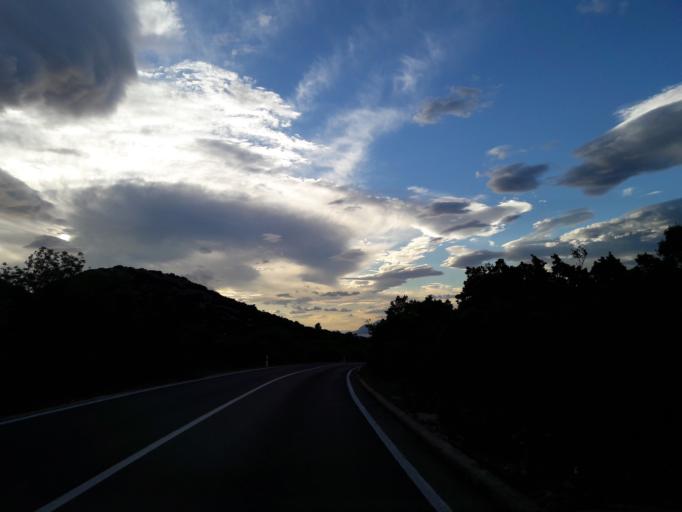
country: BA
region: Federation of Bosnia and Herzegovina
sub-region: Hercegovacko-Bosanski Kanton
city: Neum
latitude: 42.8931
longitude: 17.4962
